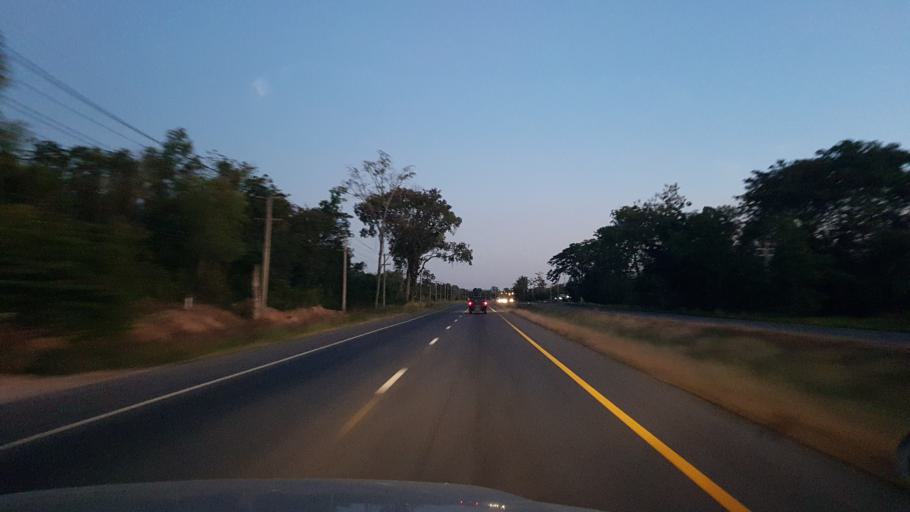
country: TH
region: Chaiyaphum
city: Phu Khiao
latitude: 16.3086
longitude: 102.2034
